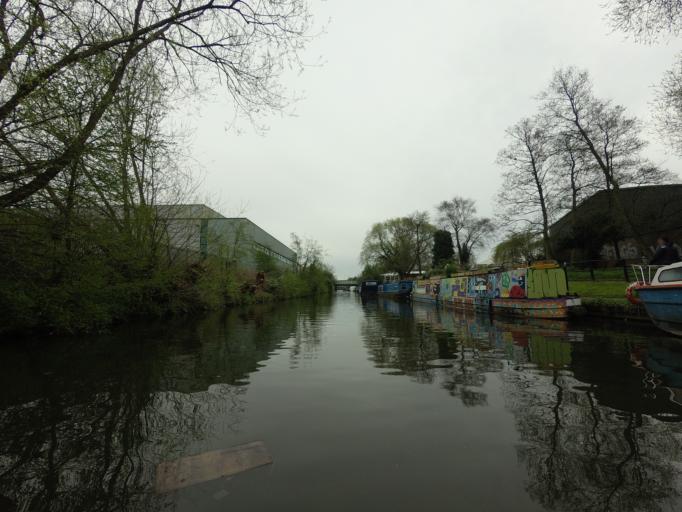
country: GB
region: England
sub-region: Greater London
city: Acton
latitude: 51.5349
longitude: -0.2627
